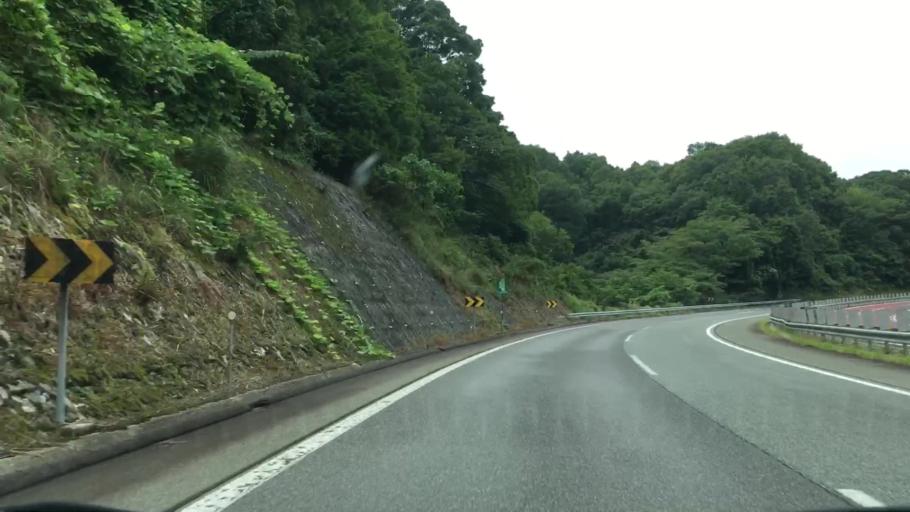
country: JP
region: Hiroshima
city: Shobara
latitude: 34.8908
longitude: 133.2245
